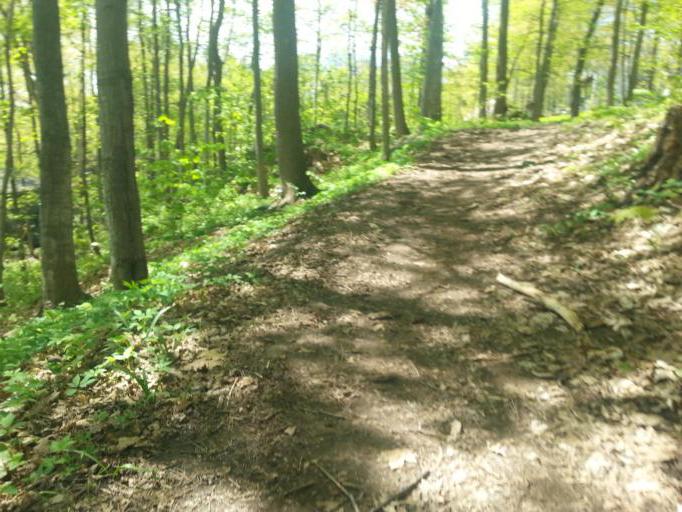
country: CA
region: Quebec
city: Quebec
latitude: 46.7689
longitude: -71.2607
